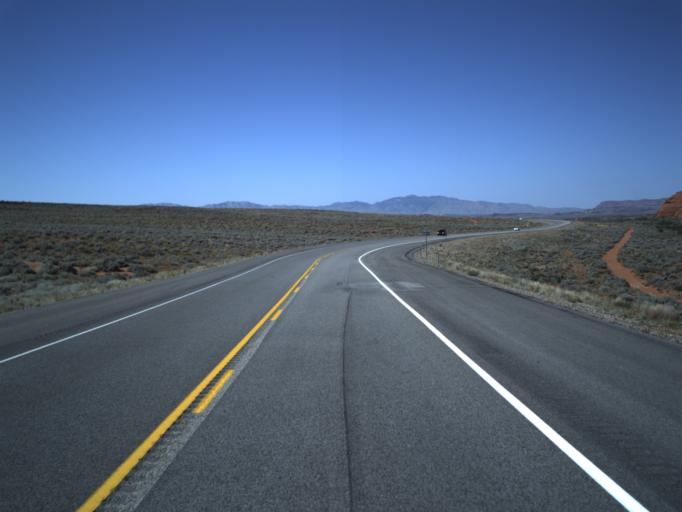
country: US
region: Utah
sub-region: Washington County
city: Washington
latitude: 37.1083
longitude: -113.4025
